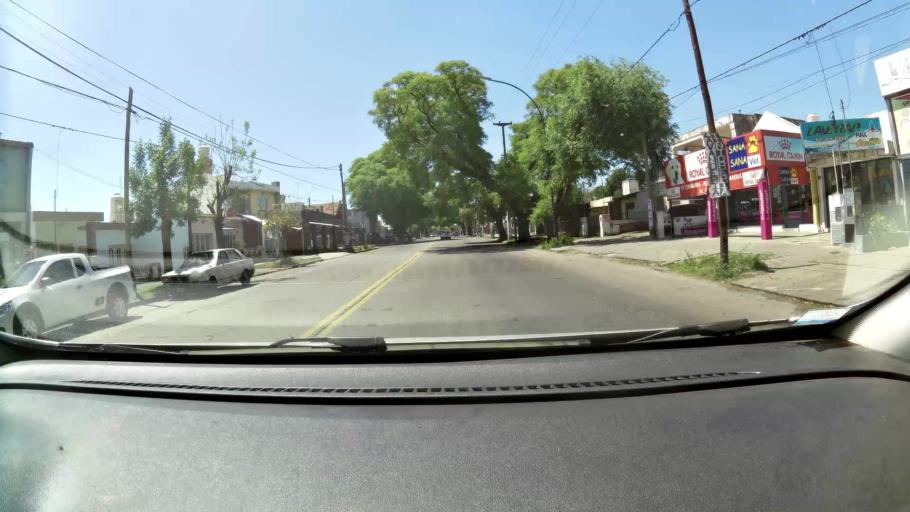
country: AR
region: Cordoba
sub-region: Departamento de Capital
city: Cordoba
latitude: -31.3780
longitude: -64.2070
